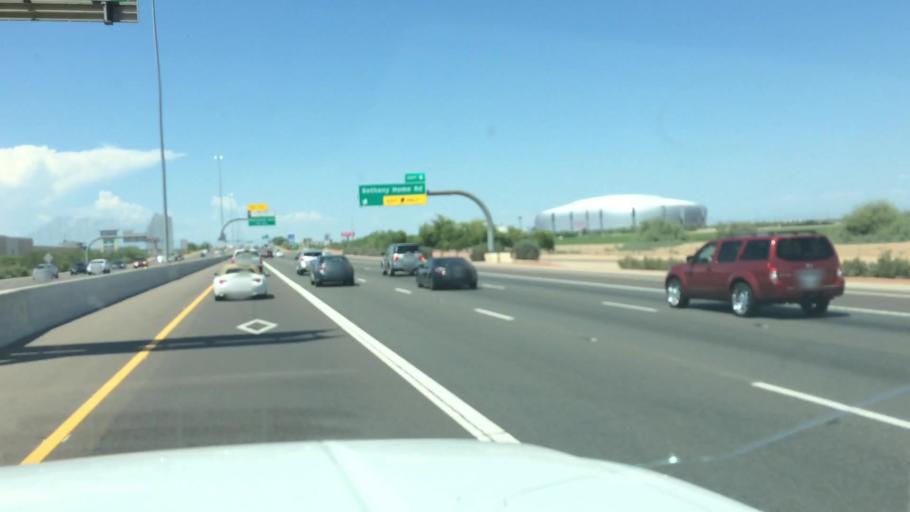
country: US
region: Arizona
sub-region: Maricopa County
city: Tolleson
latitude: 33.5156
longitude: -112.2679
